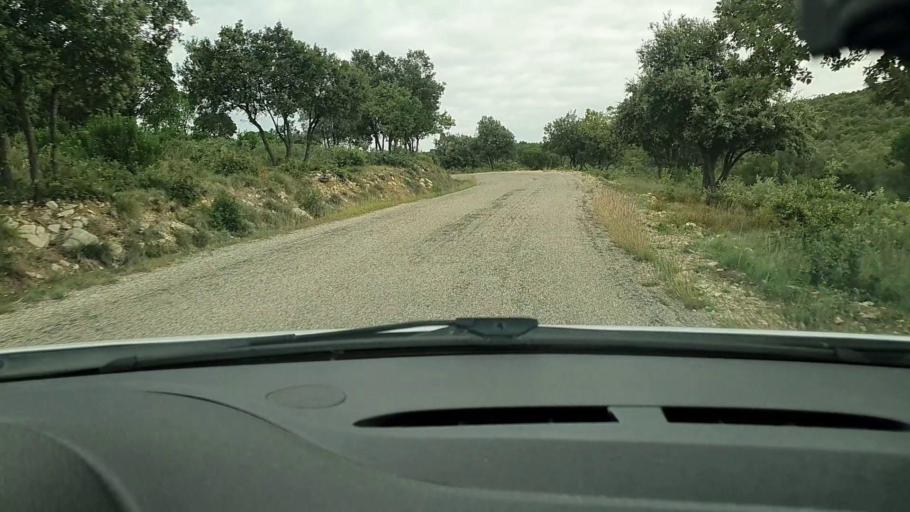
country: FR
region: Languedoc-Roussillon
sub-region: Departement du Gard
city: Montaren-et-Saint-Mediers
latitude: 44.0937
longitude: 4.2960
